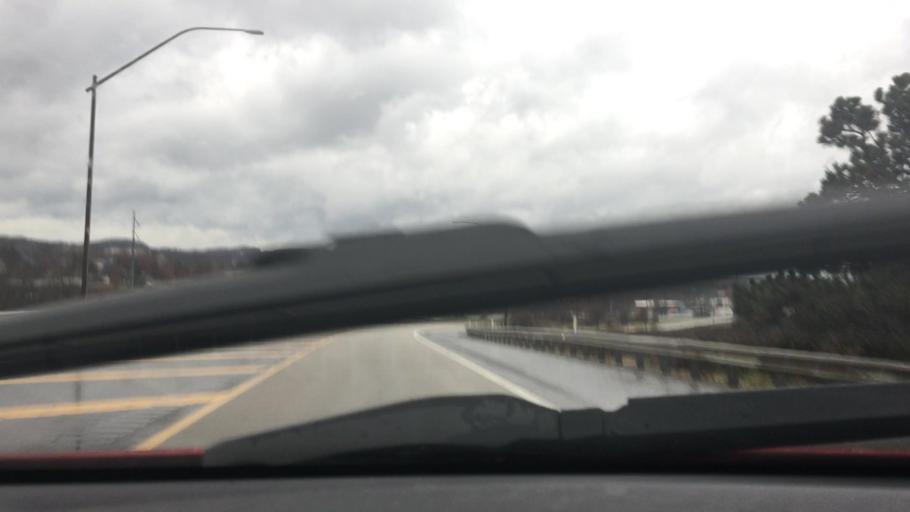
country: US
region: Pennsylvania
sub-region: Butler County
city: Cranberry Township
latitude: 40.6654
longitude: -80.0935
